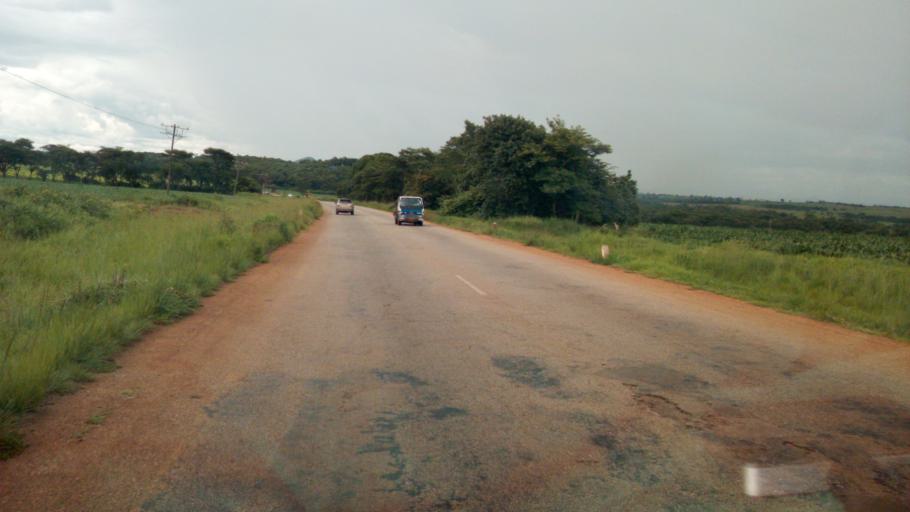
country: ZW
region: Mashonaland Central
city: Bindura
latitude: -17.3023
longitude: 31.2671
